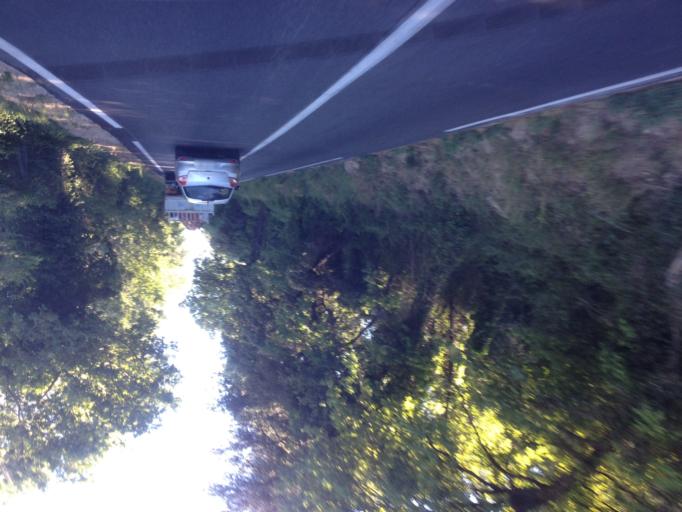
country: FR
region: Languedoc-Roussillon
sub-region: Departement du Gard
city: Montfaucon
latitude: 44.0804
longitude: 4.7775
